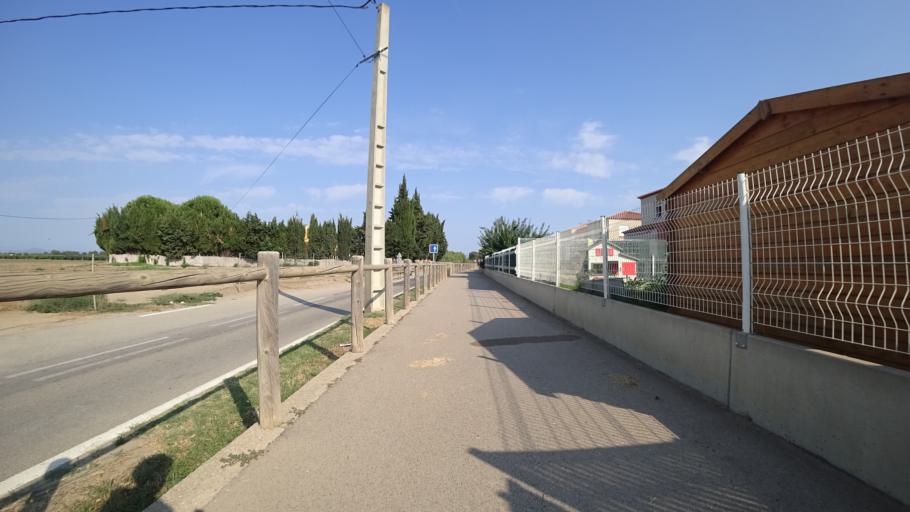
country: FR
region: Languedoc-Roussillon
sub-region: Departement des Pyrenees-Orientales
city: Saint-Laurent-de-la-Salanque
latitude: 42.7667
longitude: 2.9815
